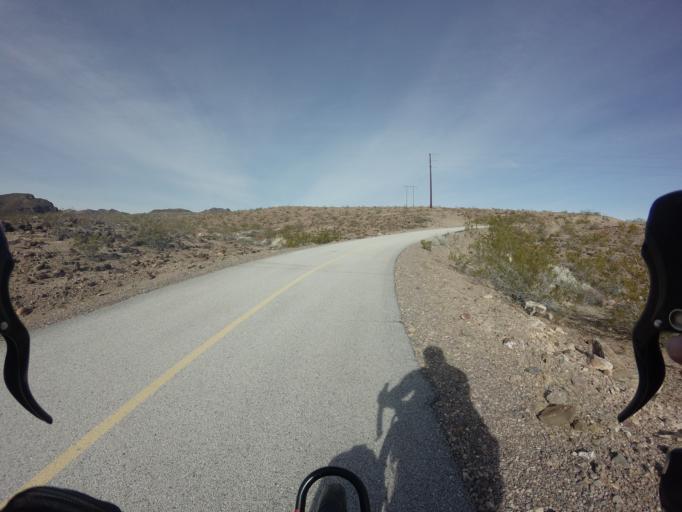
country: US
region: Nevada
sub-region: Clark County
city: Boulder City
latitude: 36.0796
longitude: -114.8255
